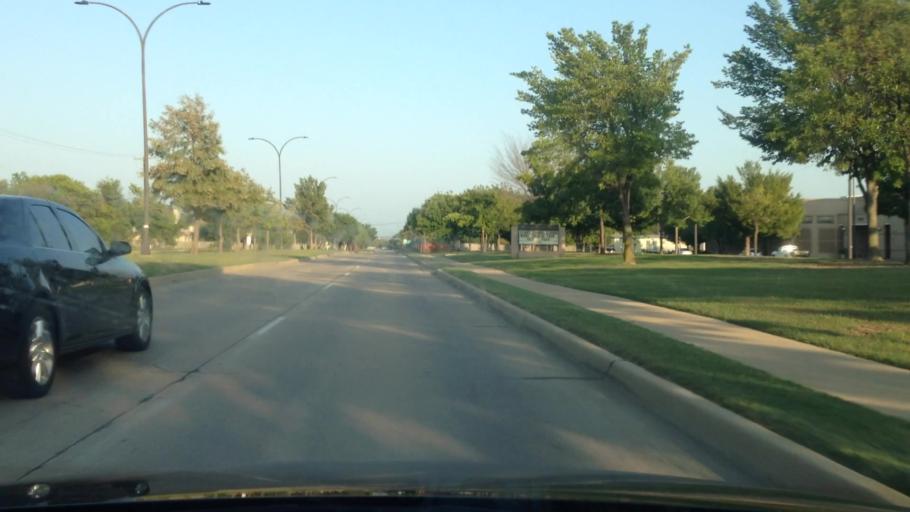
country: US
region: Texas
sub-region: Tarrant County
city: Dalworthington Gardens
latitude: 32.6566
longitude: -97.1045
